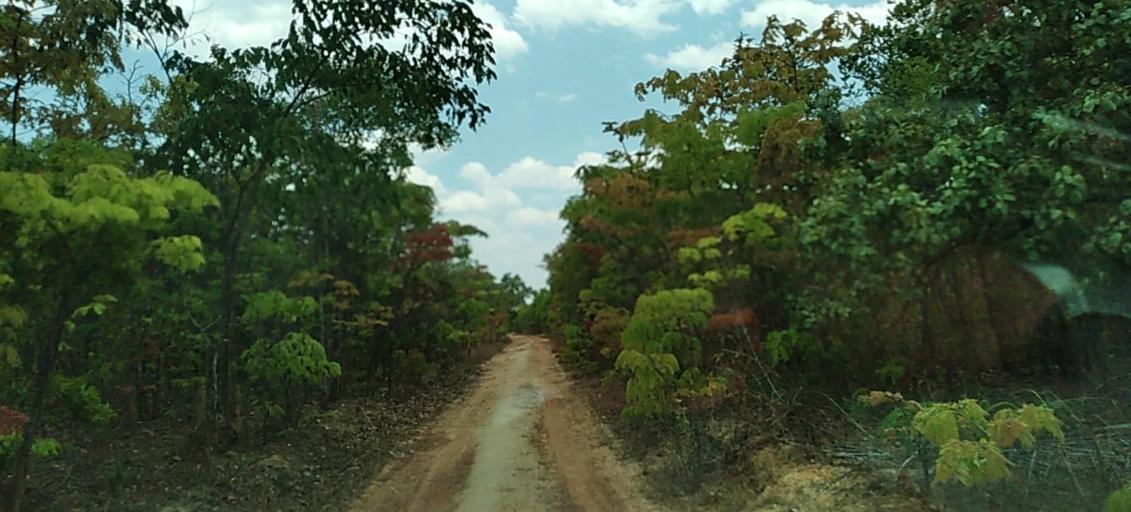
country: ZM
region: Copperbelt
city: Chililabombwe
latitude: -12.4812
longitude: 27.7008
